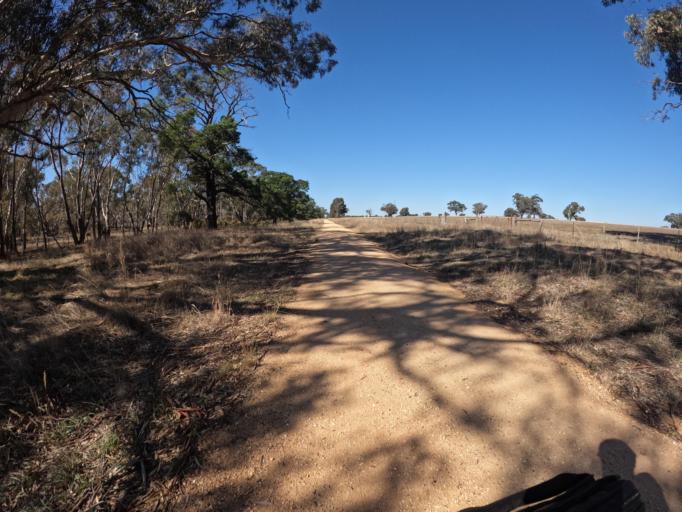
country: AU
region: Victoria
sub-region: Greater Bendigo
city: Kennington
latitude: -36.8343
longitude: 144.5955
